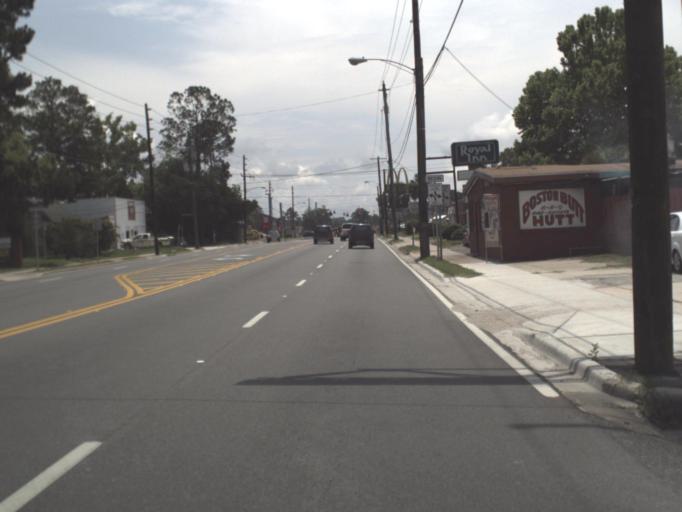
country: US
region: Florida
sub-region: Nassau County
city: Callahan
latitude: 30.5653
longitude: -81.8321
